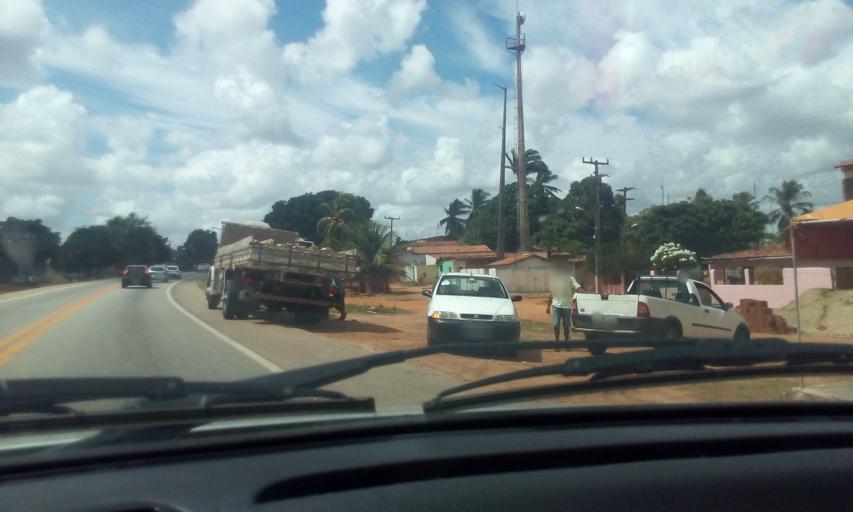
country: BR
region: Rio Grande do Norte
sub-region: Macaiba
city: Macaiba
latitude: -5.9253
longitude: -35.5378
